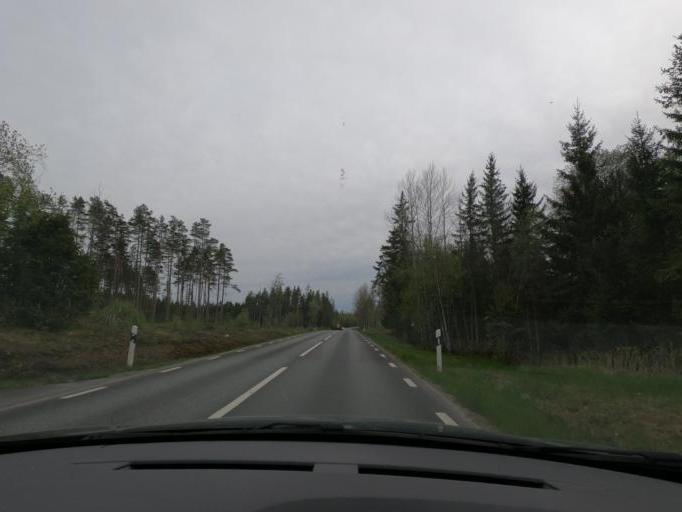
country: SE
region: Joenkoeping
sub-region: Varnamo Kommun
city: Bredaryd
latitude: 57.2097
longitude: 13.7668
